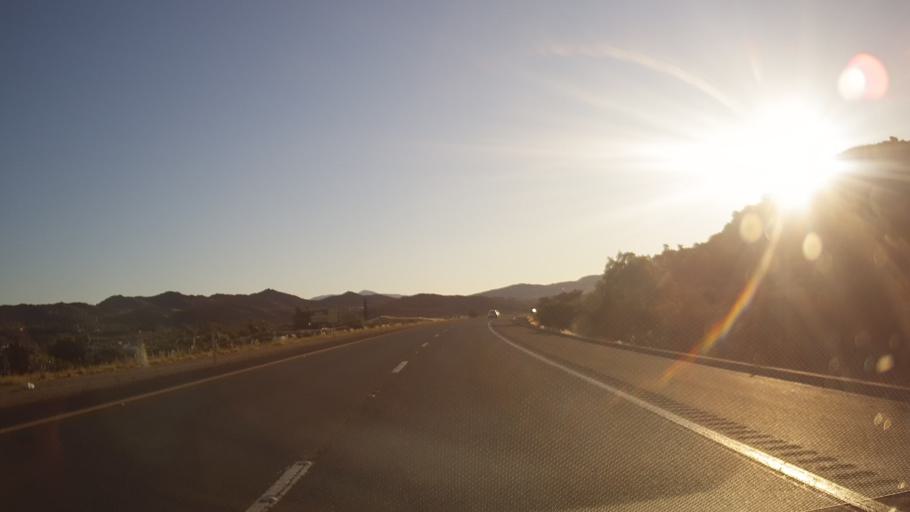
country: US
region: California
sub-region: San Diego County
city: Harbison Canyon
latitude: 32.8553
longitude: -116.8333
